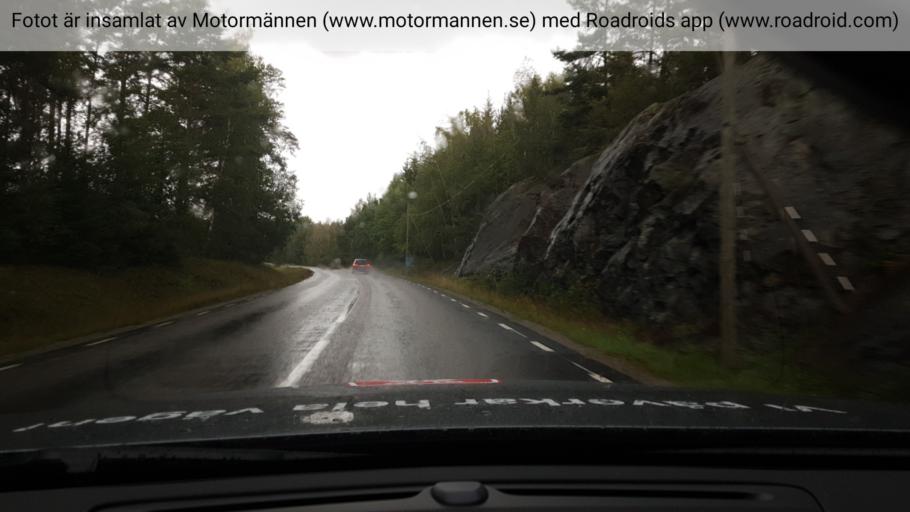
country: SE
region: Stockholm
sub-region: Nynashamns Kommun
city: Osmo
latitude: 58.9662
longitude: 17.9591
